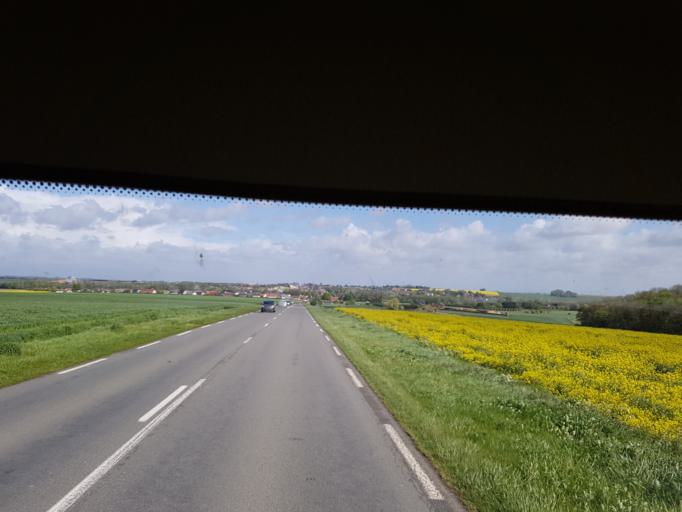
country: FR
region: Nord-Pas-de-Calais
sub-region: Departement du Nord
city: Masnieres
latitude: 50.0984
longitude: 3.2040
